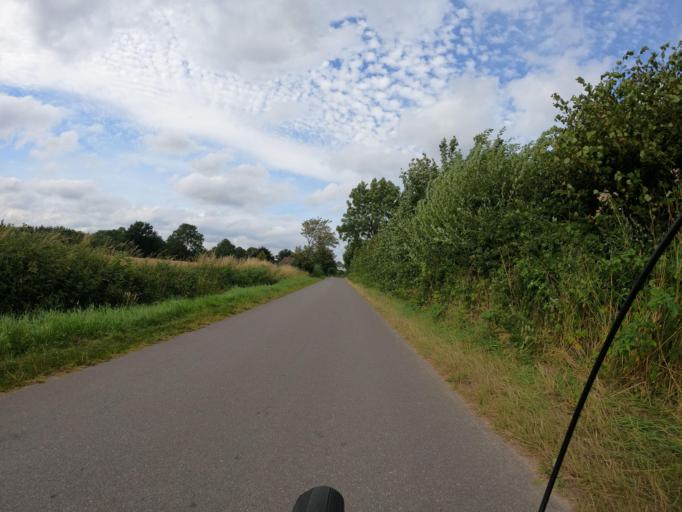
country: DE
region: Schleswig-Holstein
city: Steinberg
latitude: 54.7519
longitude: 9.7845
